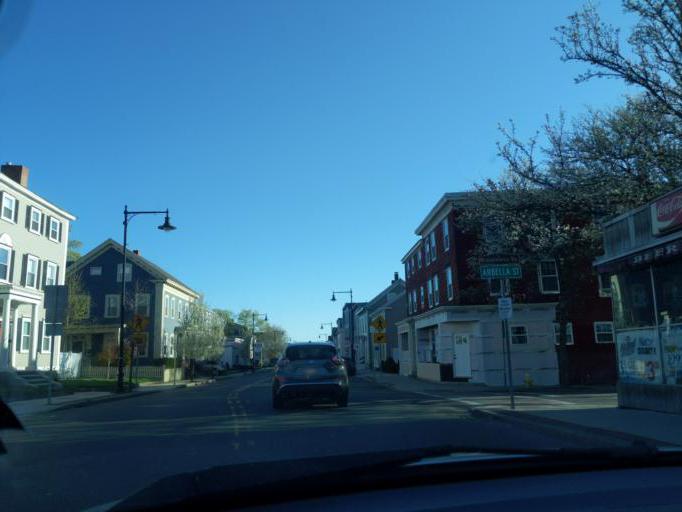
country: US
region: Massachusetts
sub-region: Essex County
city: Salem
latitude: 42.5286
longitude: -70.8901
